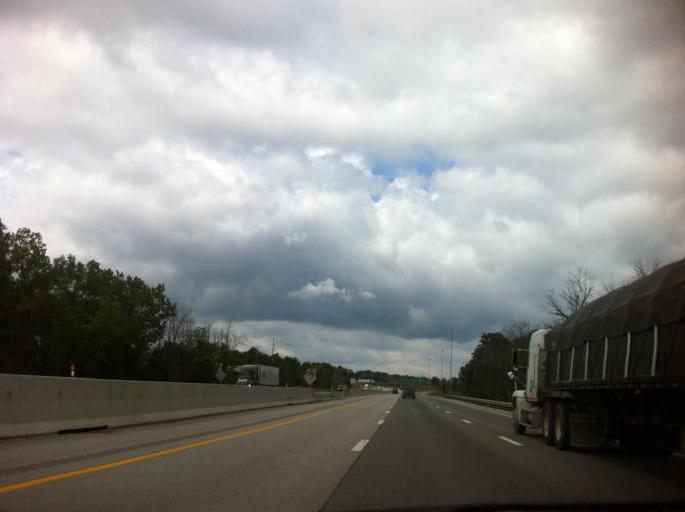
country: US
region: Ohio
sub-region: Summit County
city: Boston Heights
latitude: 41.2570
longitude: -81.4845
